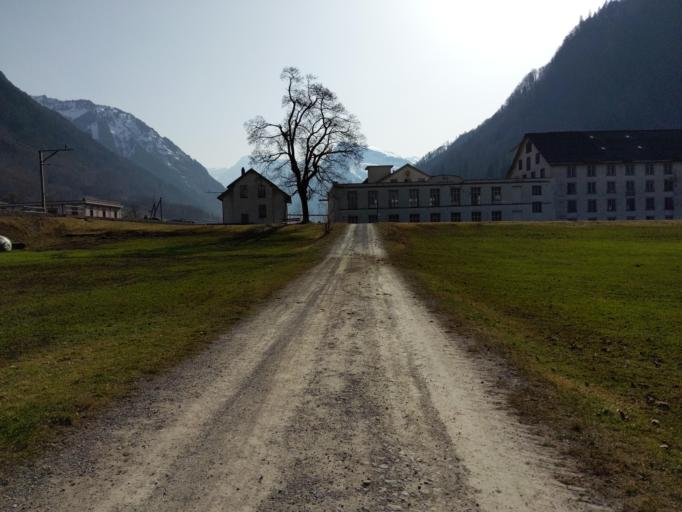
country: CH
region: Glarus
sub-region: Glarus
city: Luchsingen
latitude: 46.9519
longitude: 9.0295
